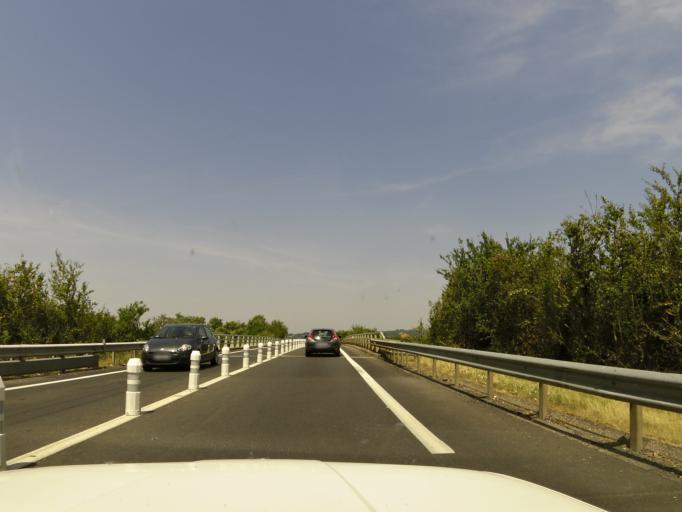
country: FR
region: Rhone-Alpes
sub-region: Departement de l'Ain
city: Saint-Maurice-de-Gourdans
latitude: 45.8618
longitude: 5.1777
